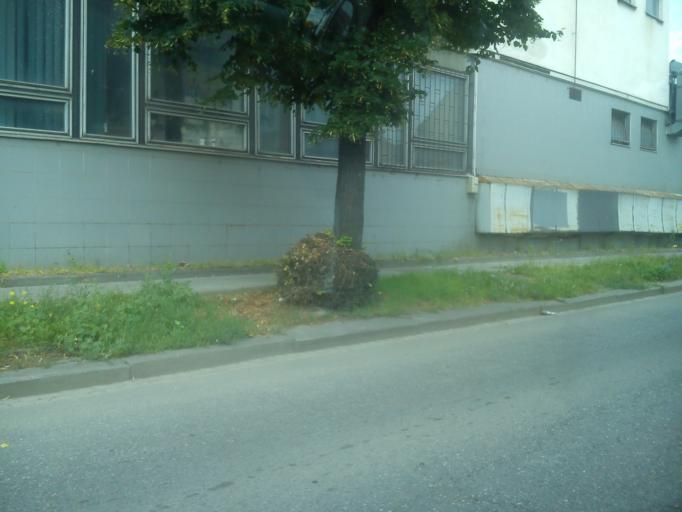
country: CZ
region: South Moravian
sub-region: Mesto Brno
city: Brno
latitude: 49.1857
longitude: 16.6179
